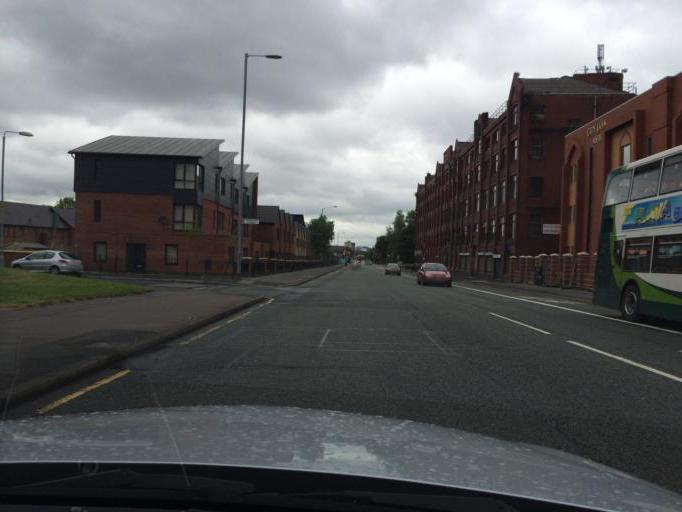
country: GB
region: England
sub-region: Manchester
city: Longsight
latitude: 53.4614
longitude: -2.2077
